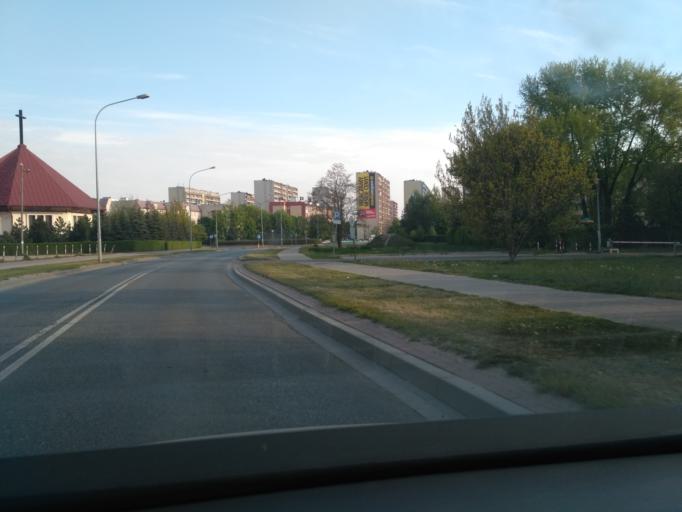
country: PL
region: Masovian Voivodeship
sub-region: Siedlce
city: Siedlce
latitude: 52.1623
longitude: 22.2882
